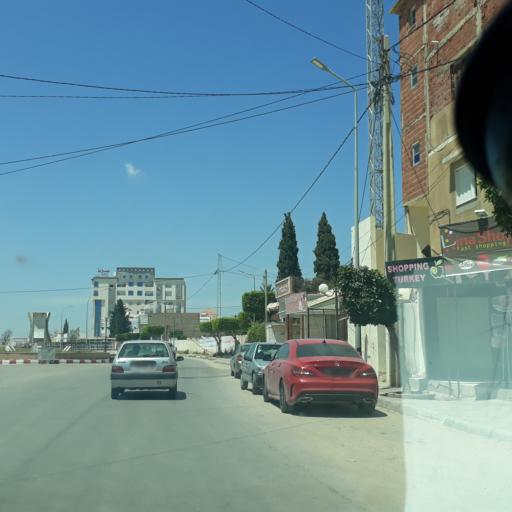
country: TN
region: Safaqis
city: Al Qarmadah
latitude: 34.8044
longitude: 10.7584
